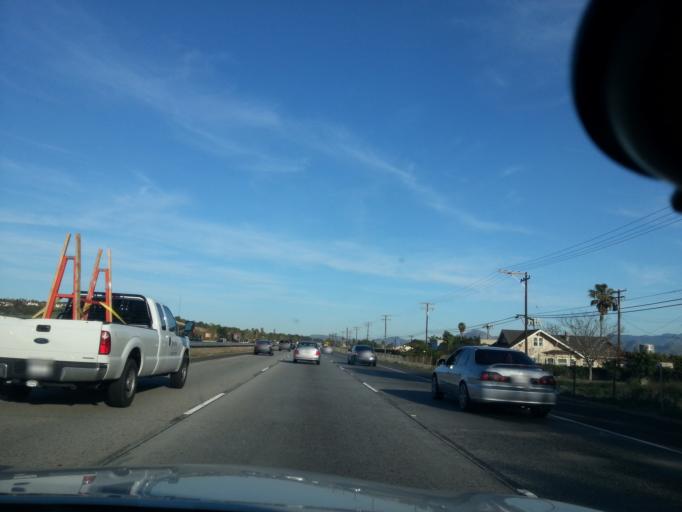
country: US
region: California
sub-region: Ventura County
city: El Rio
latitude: 34.2219
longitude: -119.1146
